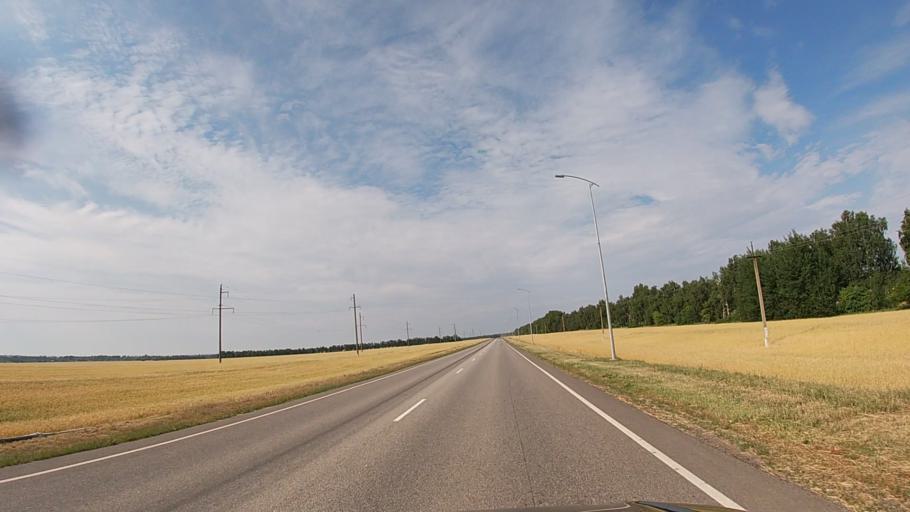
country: RU
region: Belgorod
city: Proletarskiy
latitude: 50.8206
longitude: 35.7567
